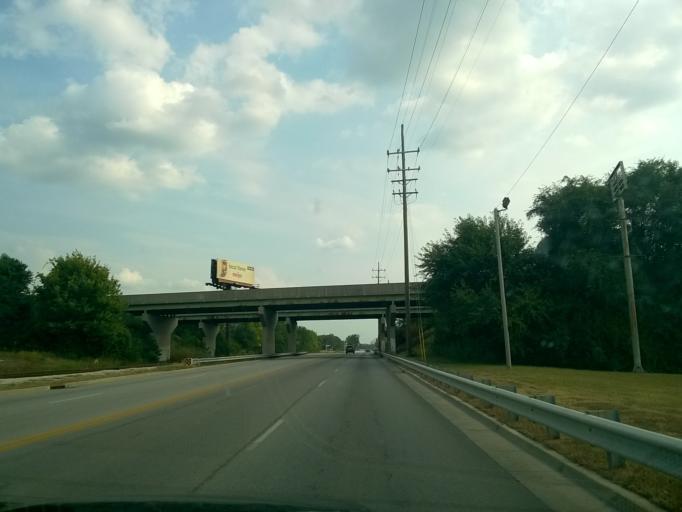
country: US
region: Indiana
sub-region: Vigo County
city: Terre Haute
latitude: 39.4309
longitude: -87.3943
